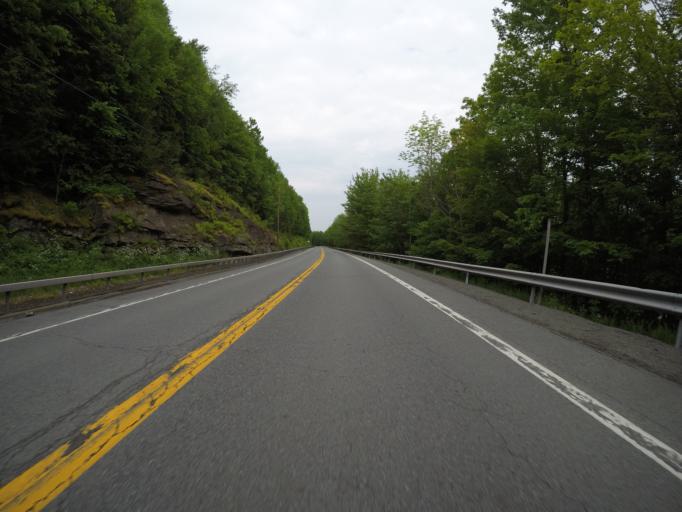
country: US
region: New York
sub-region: Sullivan County
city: Livingston Manor
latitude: 42.0747
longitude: -74.8423
